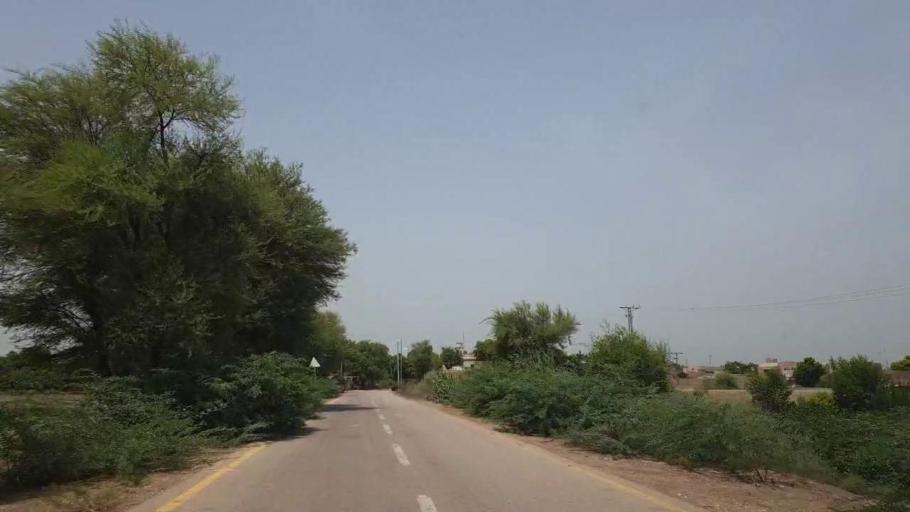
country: PK
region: Sindh
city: Sakrand
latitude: 26.2025
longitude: 68.2435
